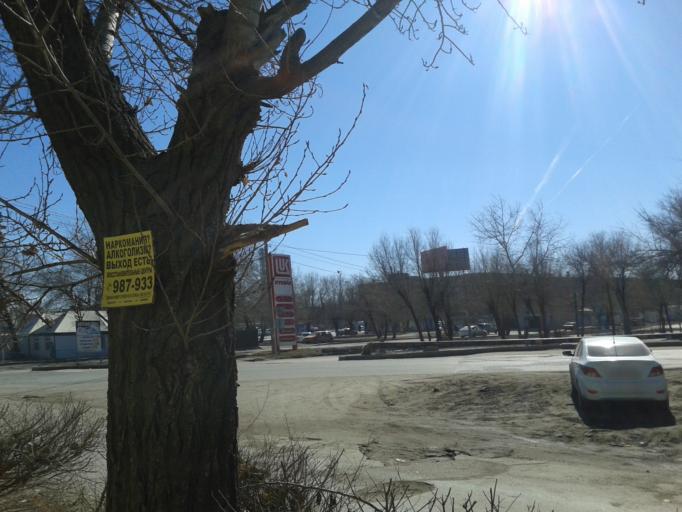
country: RU
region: Volgograd
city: Krasnoslobodsk
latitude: 48.7522
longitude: 44.5482
